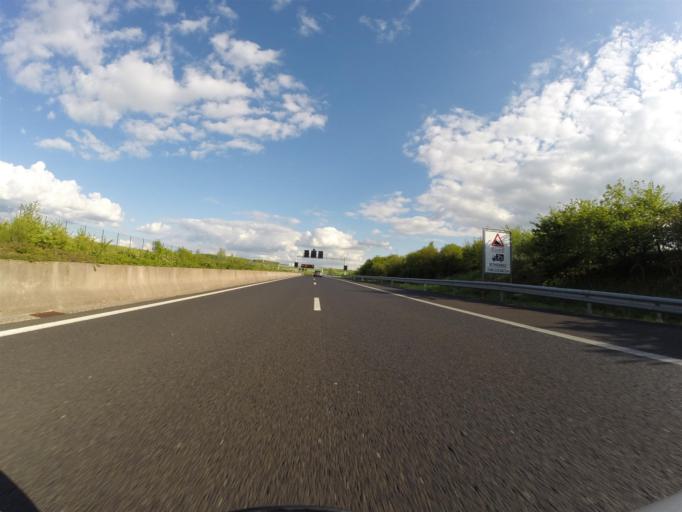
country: LU
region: Grevenmacher
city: Schengen
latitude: 49.4860
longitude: 6.3347
